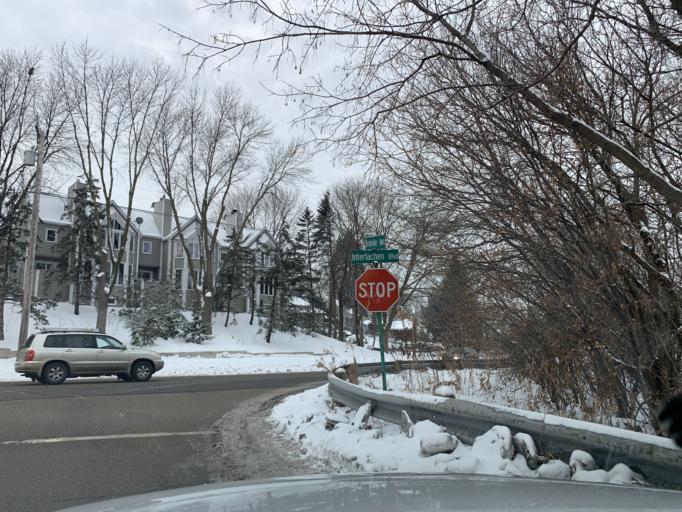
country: US
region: Minnesota
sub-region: Hennepin County
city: Edina
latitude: 44.9132
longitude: -93.3549
